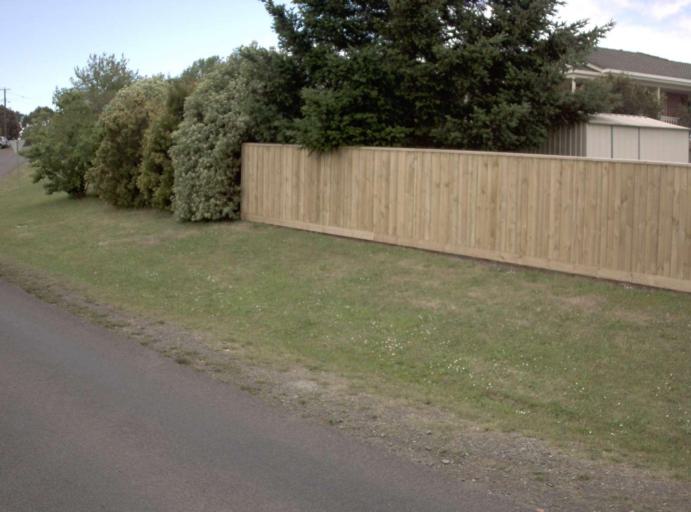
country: AU
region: Victoria
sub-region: Baw Baw
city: Warragul
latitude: -38.1415
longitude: 145.9384
